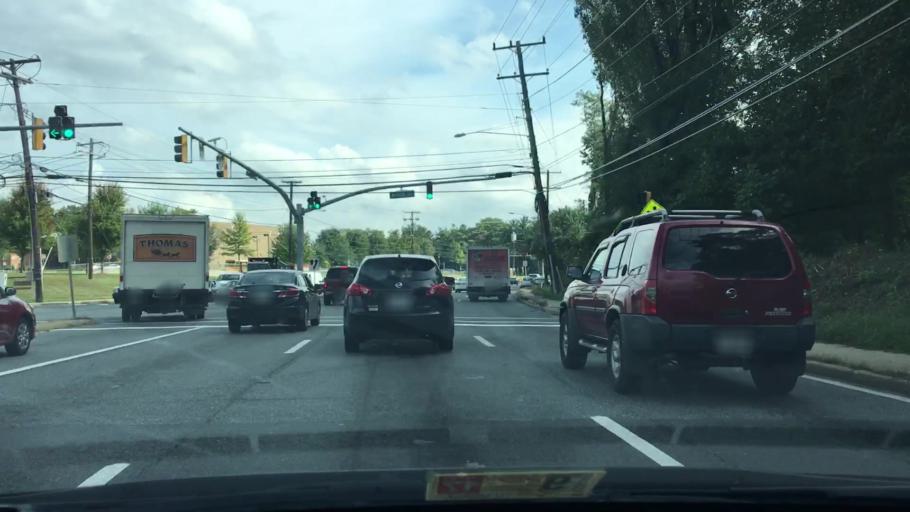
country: US
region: Maryland
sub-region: Montgomery County
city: Kemp Mill
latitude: 39.0357
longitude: -77.0263
